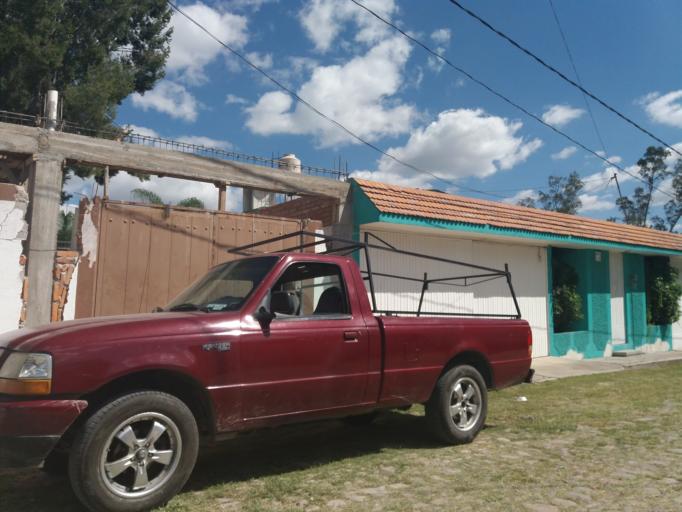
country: MX
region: Aguascalientes
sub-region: Aguascalientes
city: San Sebastian [Fraccionamiento]
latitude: 21.7858
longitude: -102.2782
